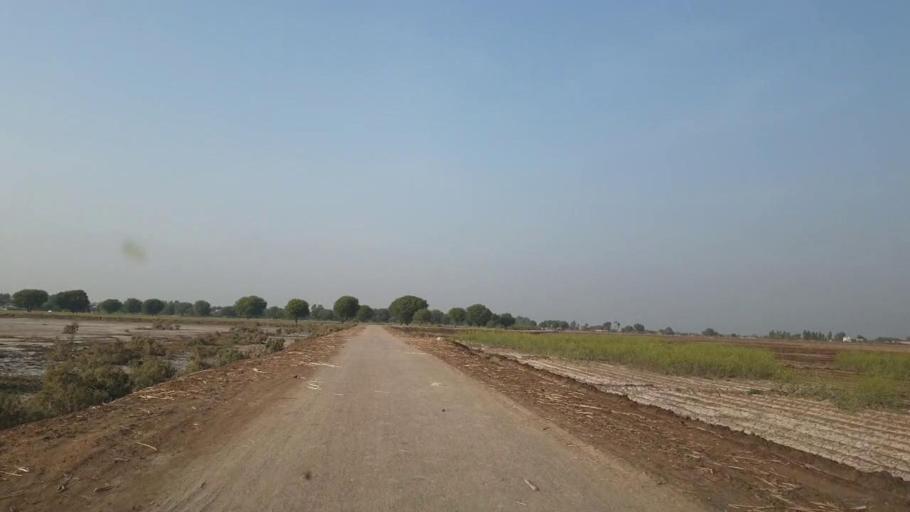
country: PK
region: Sindh
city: Pithoro
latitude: 25.6719
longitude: 69.2038
